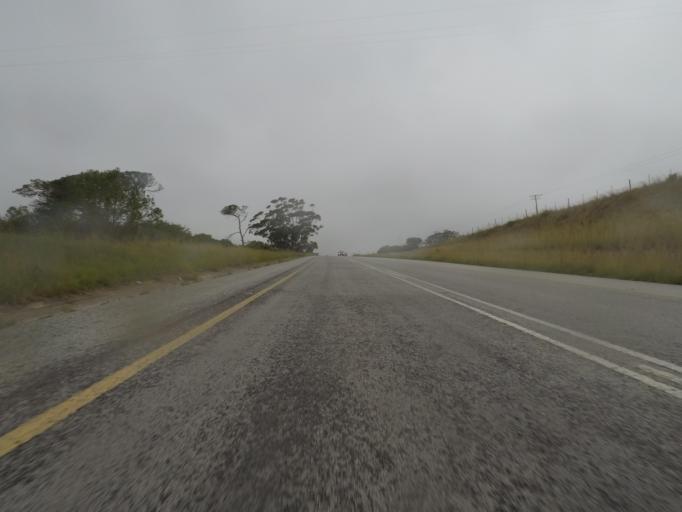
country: ZA
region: Eastern Cape
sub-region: Cacadu District Municipality
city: Grahamstown
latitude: -33.6384
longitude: 26.3236
